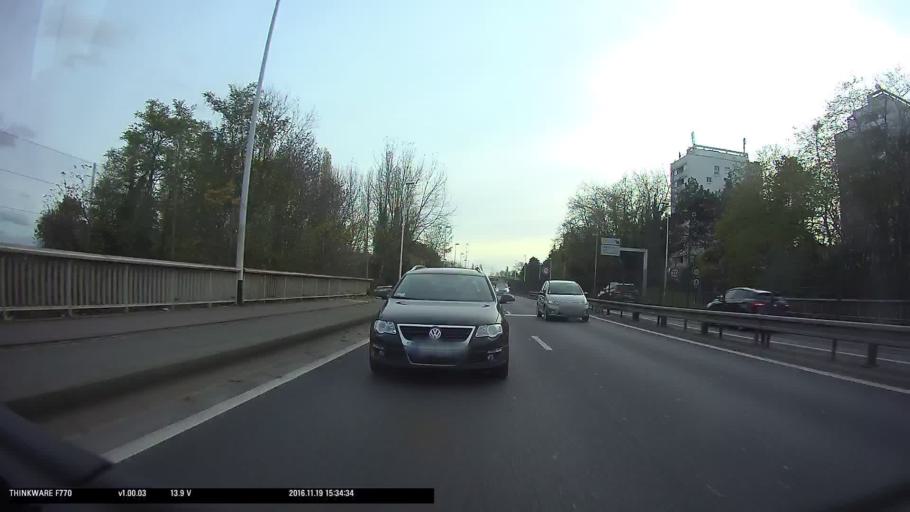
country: FR
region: Ile-de-France
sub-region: Departement du Val-d'Oise
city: Cergy-Pontoise
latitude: 49.0521
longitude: 2.0815
